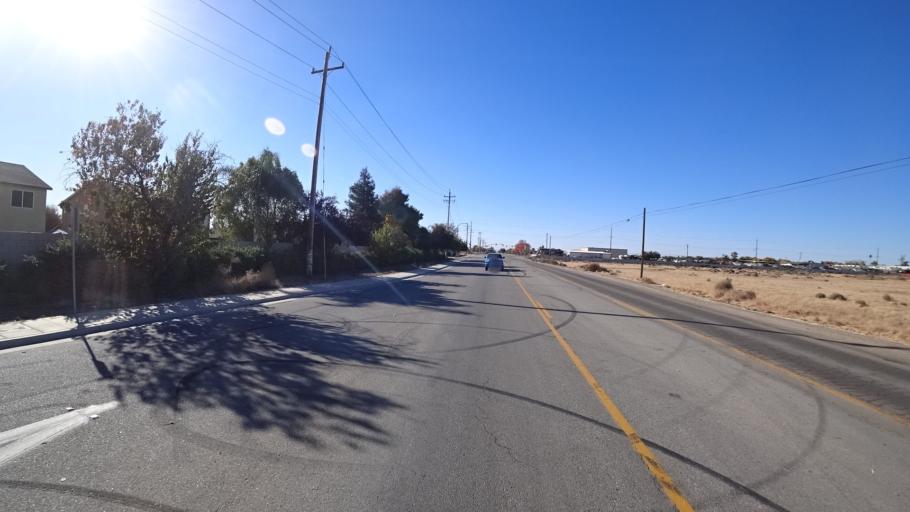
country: US
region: California
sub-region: Kern County
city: Greenfield
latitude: 35.2813
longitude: -119.0003
